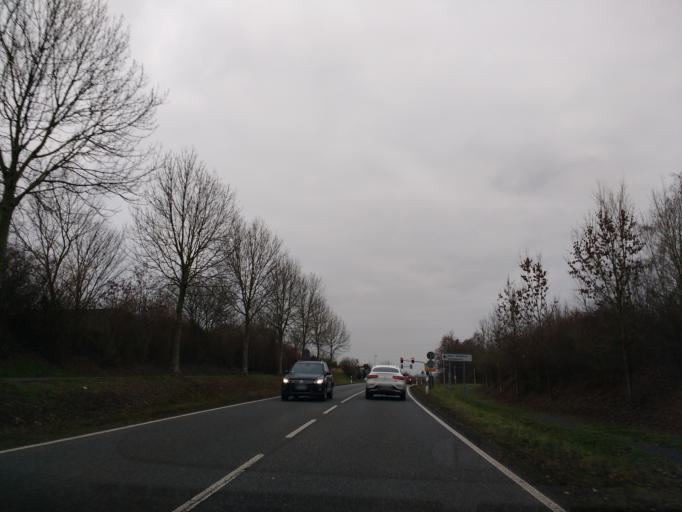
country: DE
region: Hesse
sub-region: Regierungsbezirk Kassel
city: Baunatal
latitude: 51.2508
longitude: 9.3979
